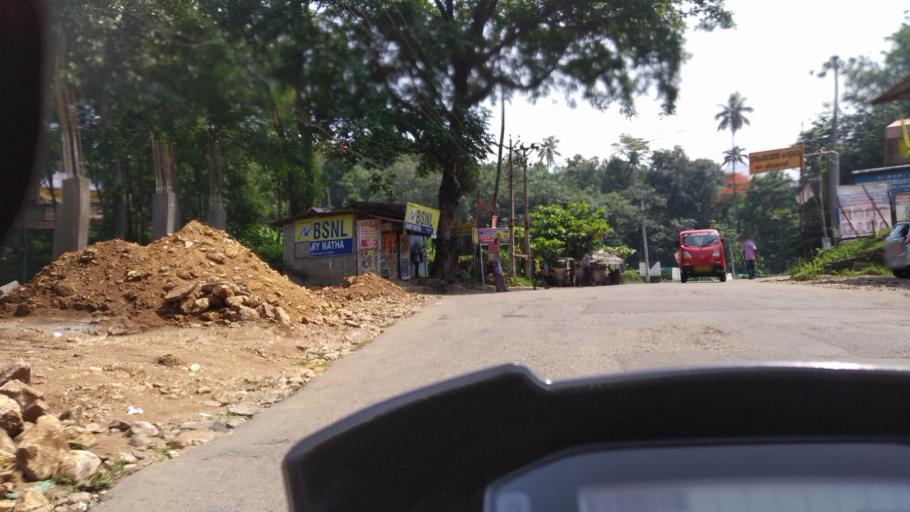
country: IN
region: Kerala
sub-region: Kottayam
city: Erattupetta
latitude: 9.6990
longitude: 76.8053
